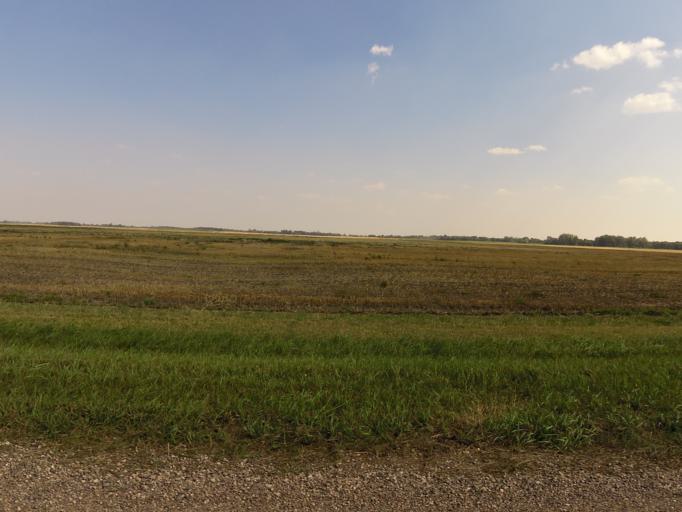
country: US
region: North Dakota
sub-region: Walsh County
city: Grafton
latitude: 48.4321
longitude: -97.3972
